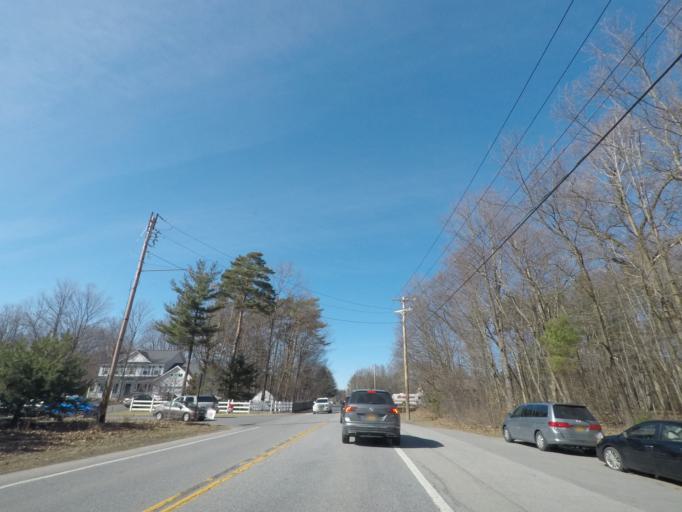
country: US
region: New York
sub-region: Saratoga County
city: Milton
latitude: 43.0309
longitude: -73.8483
